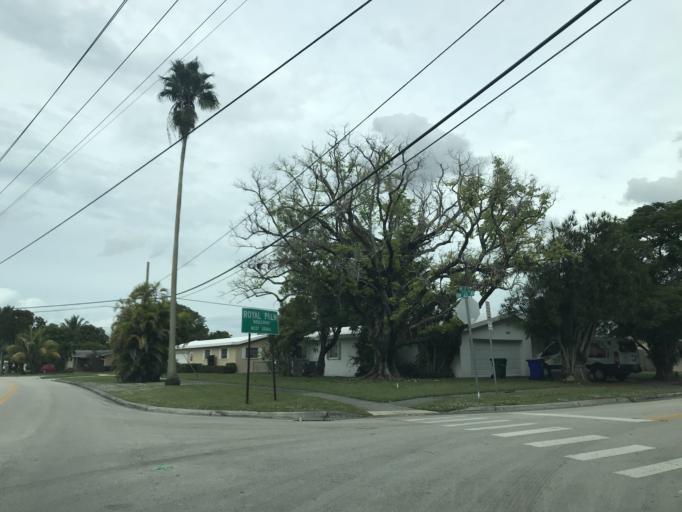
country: US
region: Florida
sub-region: Broward County
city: Margate
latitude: 26.2512
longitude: -80.2118
